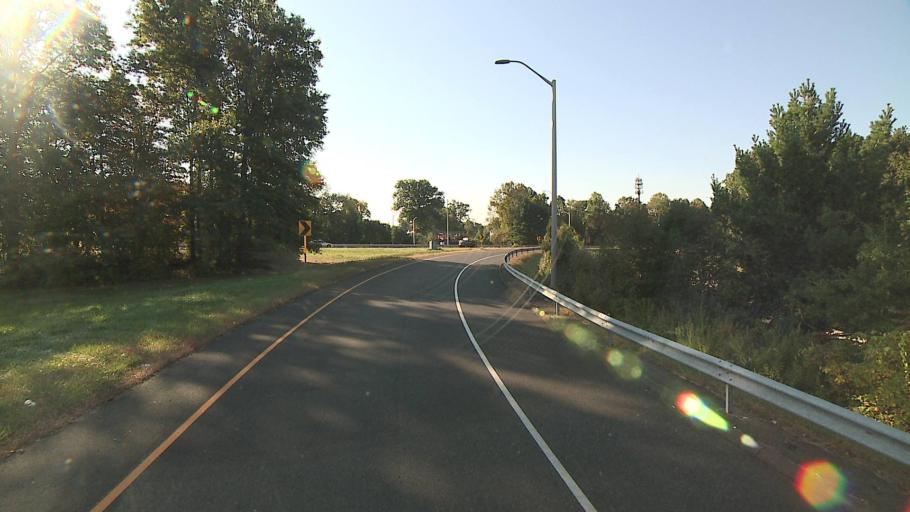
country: US
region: Connecticut
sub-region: New Haven County
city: City of Milford (balance)
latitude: 41.2508
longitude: -73.0779
